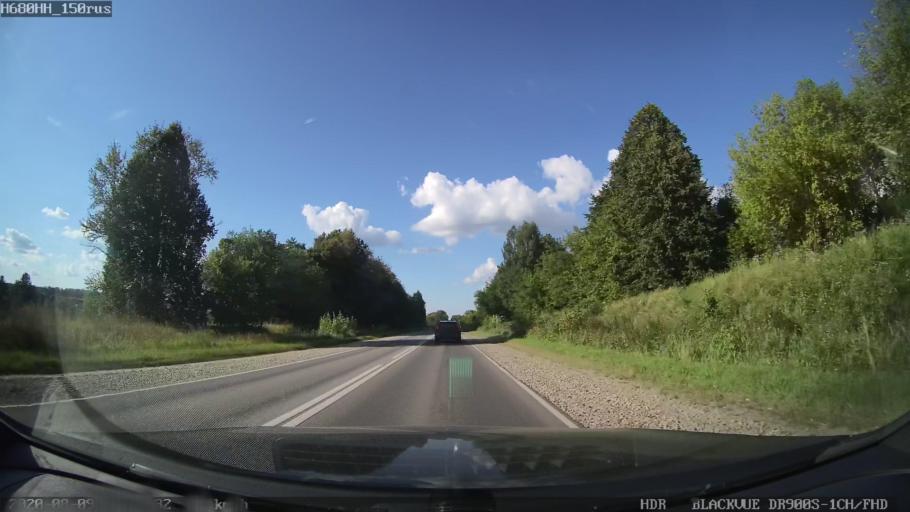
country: RU
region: Tula
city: Zaokskiy
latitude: 54.7748
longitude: 37.4354
